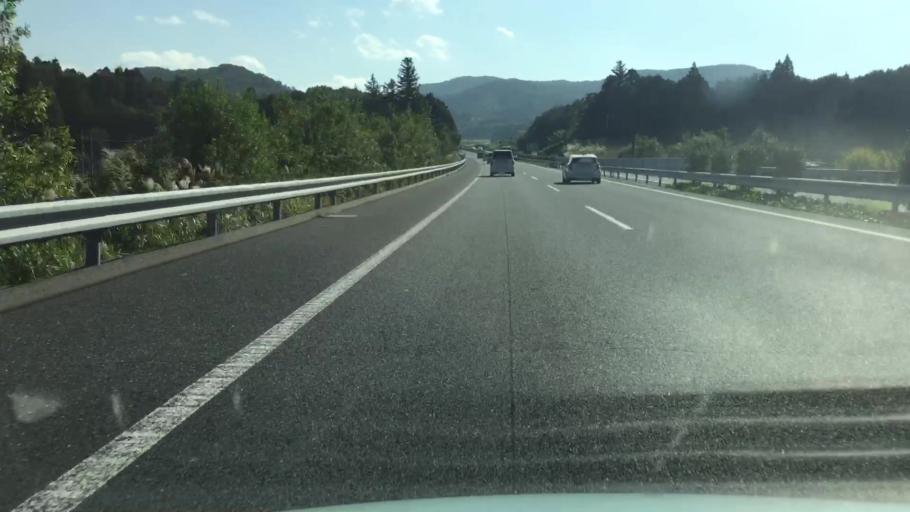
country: JP
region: Ibaraki
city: Iwase
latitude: 36.3443
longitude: 140.1793
